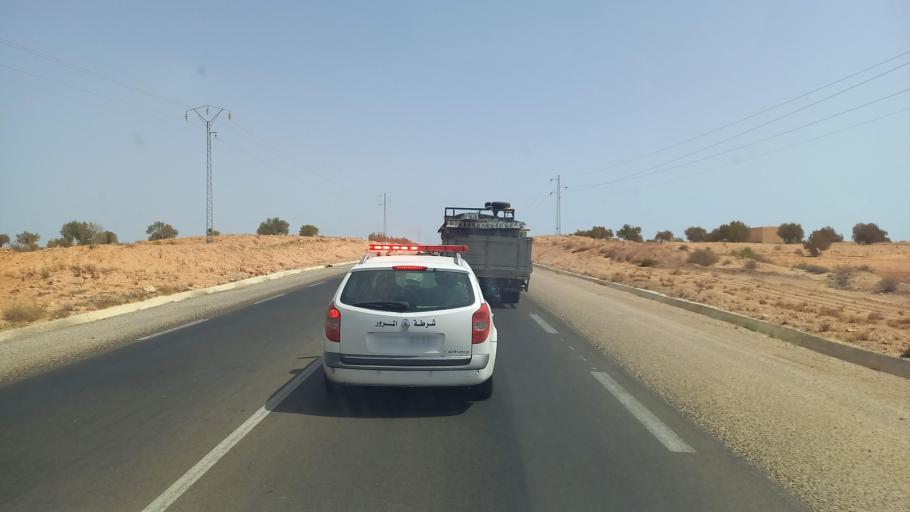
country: TN
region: Madanin
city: Zarzis
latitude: 33.4149
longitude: 10.8707
